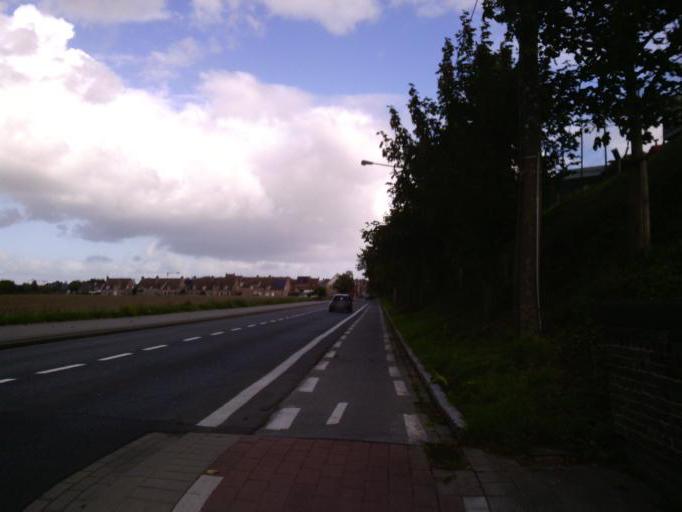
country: BE
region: Flanders
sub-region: Provincie West-Vlaanderen
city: Kortrijk
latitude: 50.8177
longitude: 3.2432
